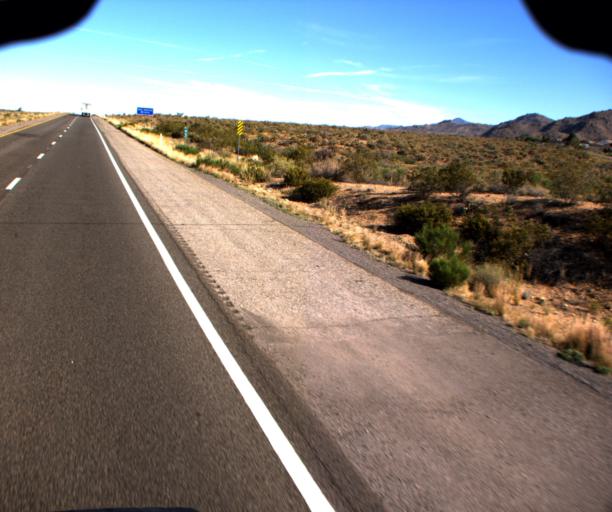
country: US
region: Arizona
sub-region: Mohave County
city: Golden Valley
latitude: 35.2438
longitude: -114.1482
